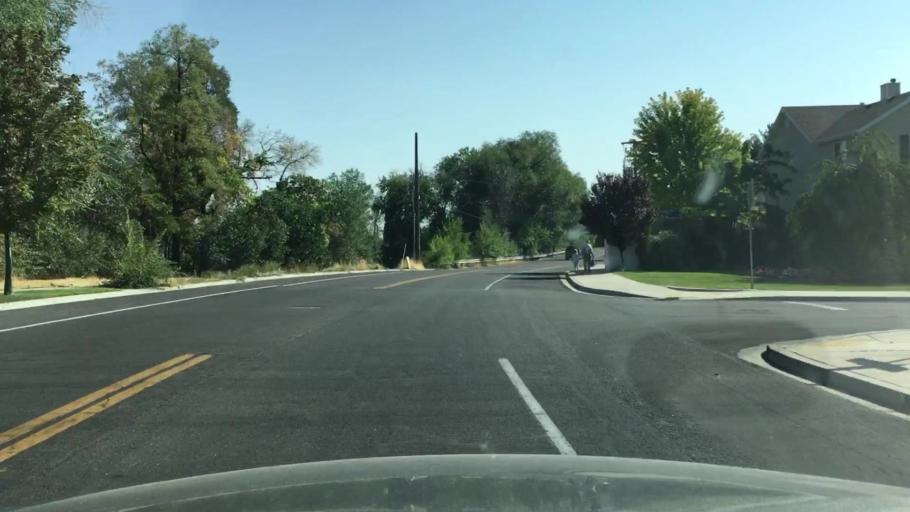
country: US
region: Utah
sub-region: Utah County
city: Provo
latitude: 40.2630
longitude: -111.6711
